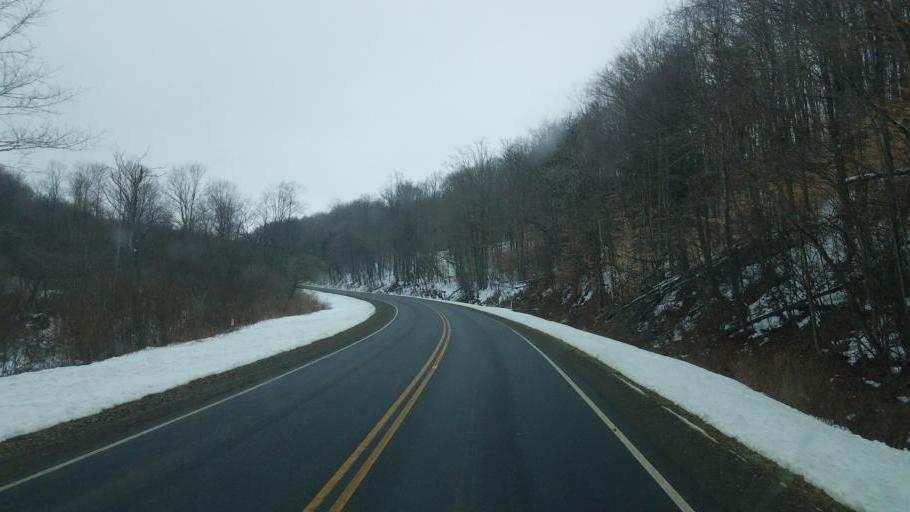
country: US
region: New York
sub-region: Allegany County
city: Andover
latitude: 42.0203
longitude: -77.7535
